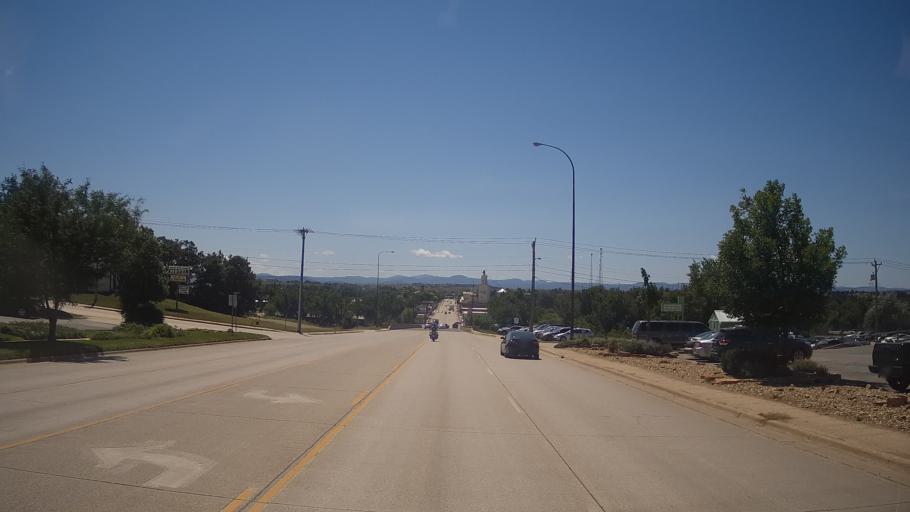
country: US
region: South Dakota
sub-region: Butte County
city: Belle Fourche
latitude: 44.6778
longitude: -103.8537
